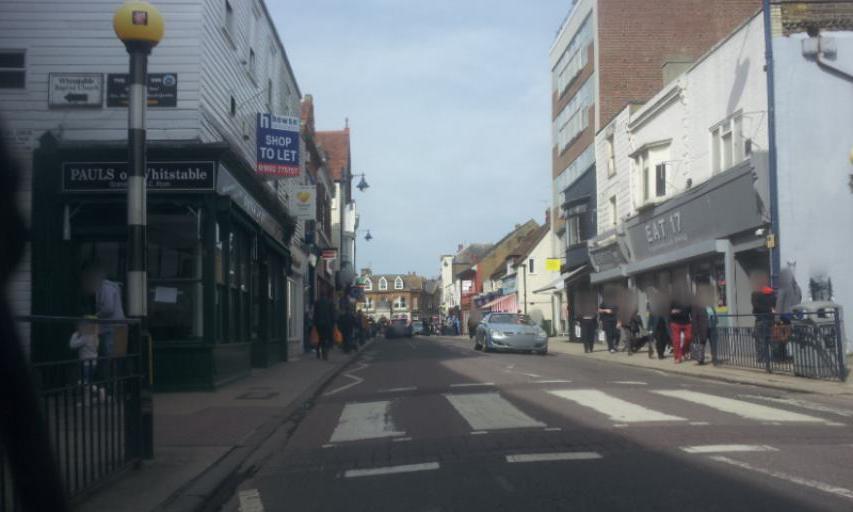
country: GB
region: England
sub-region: Kent
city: Whitstable
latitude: 51.3591
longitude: 1.0244
